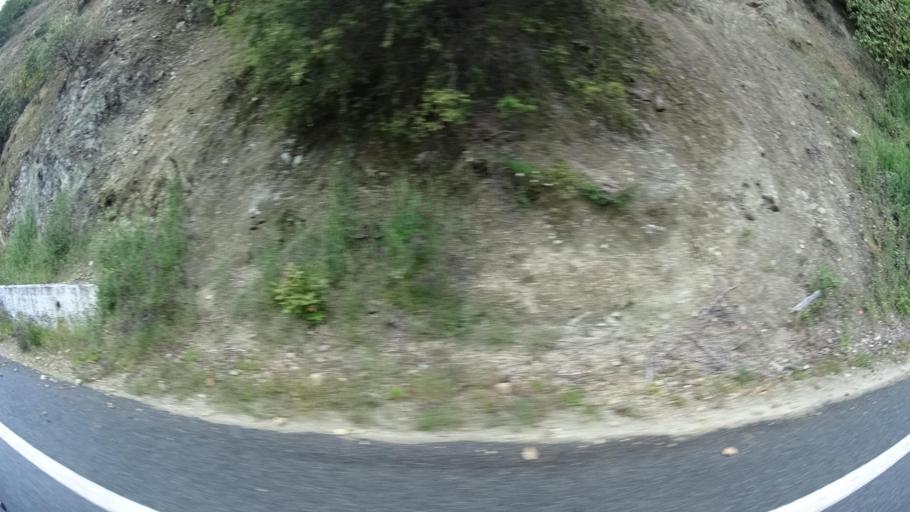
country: US
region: California
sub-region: Humboldt County
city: Willow Creek
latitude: 41.2558
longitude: -123.6239
